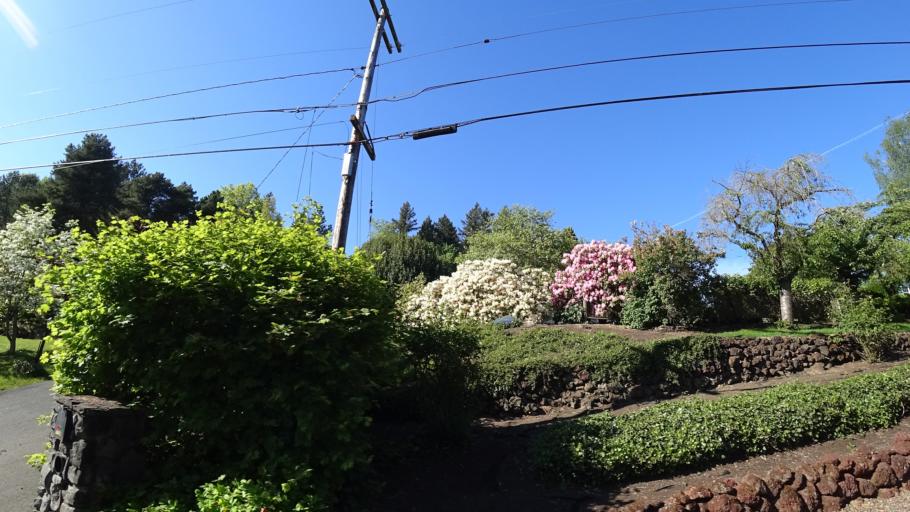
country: US
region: Oregon
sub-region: Washington County
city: West Slope
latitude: 45.4961
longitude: -122.7561
